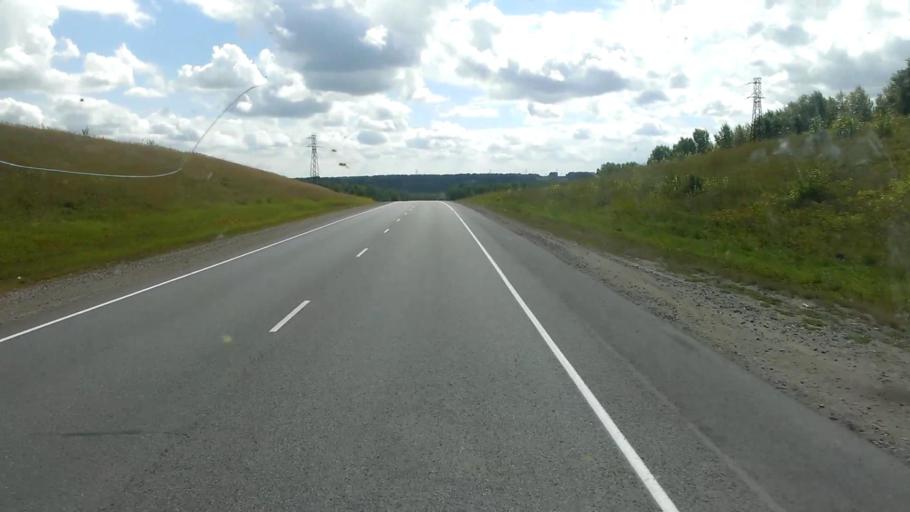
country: RU
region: Altai Krai
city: Troitskoye
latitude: 52.9449
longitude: 84.7746
